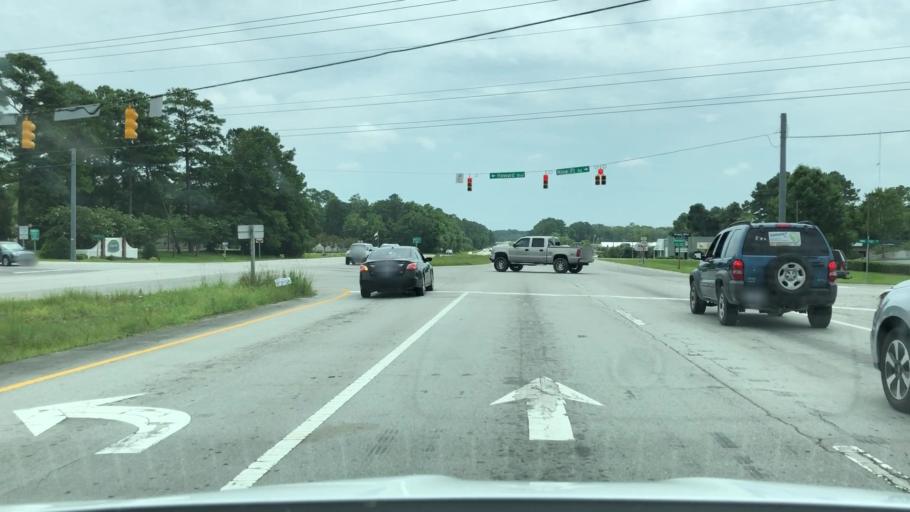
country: US
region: North Carolina
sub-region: Carteret County
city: Newport
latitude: 34.7896
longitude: -76.8765
